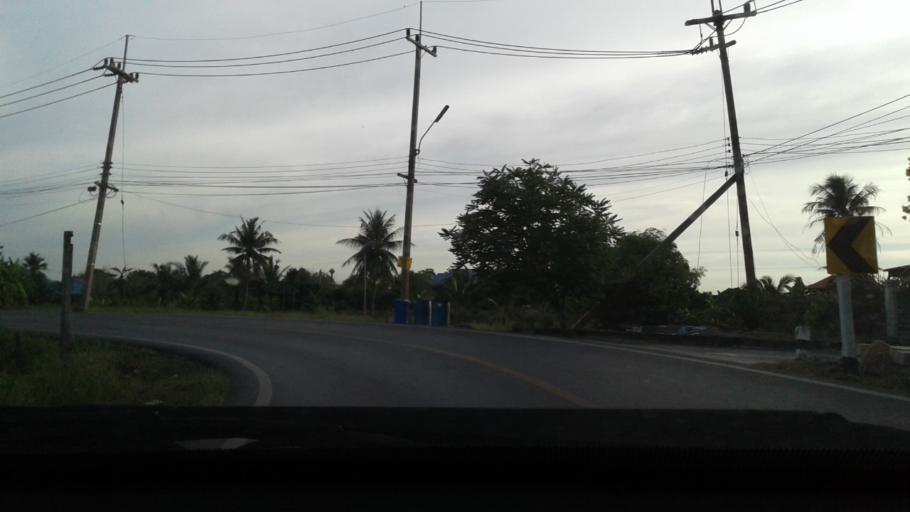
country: TH
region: Nonthaburi
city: Sai Noi
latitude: 13.9186
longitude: 100.2544
